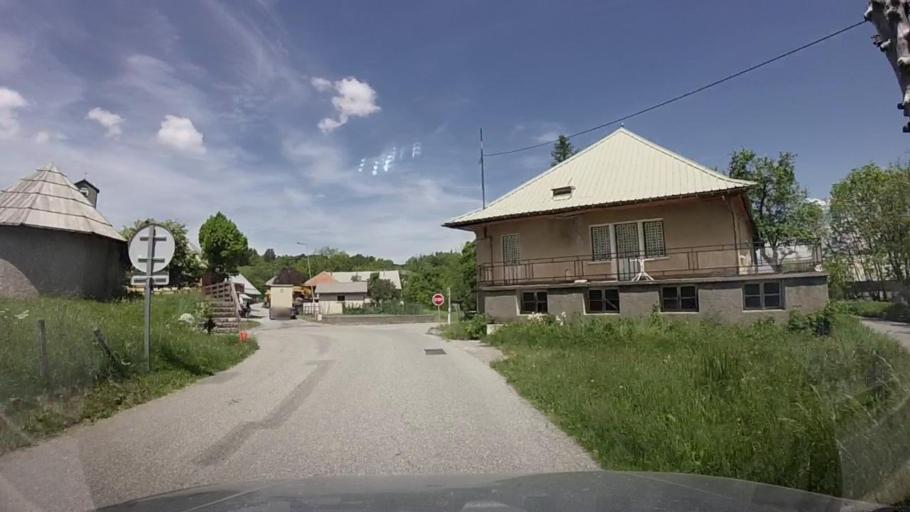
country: FR
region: Provence-Alpes-Cote d'Azur
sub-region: Departement des Alpes-de-Haute-Provence
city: Seyne-les-Alpes
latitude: 44.4148
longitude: 6.3512
